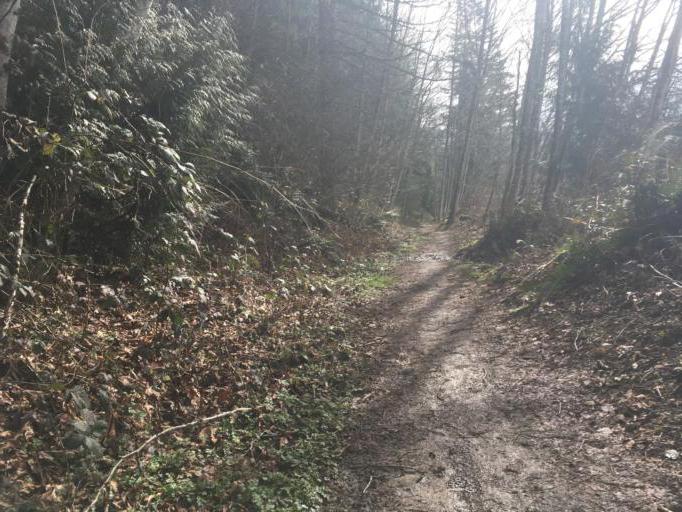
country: US
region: Washington
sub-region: Whatcom County
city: Sudden Valley
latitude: 48.6934
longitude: -122.2940
